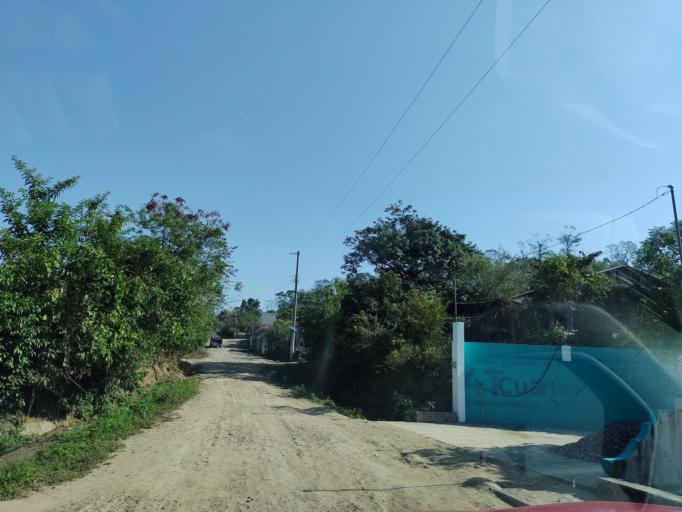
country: MX
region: Veracruz
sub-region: Papantla
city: Polutla
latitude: 20.5172
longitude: -97.2441
